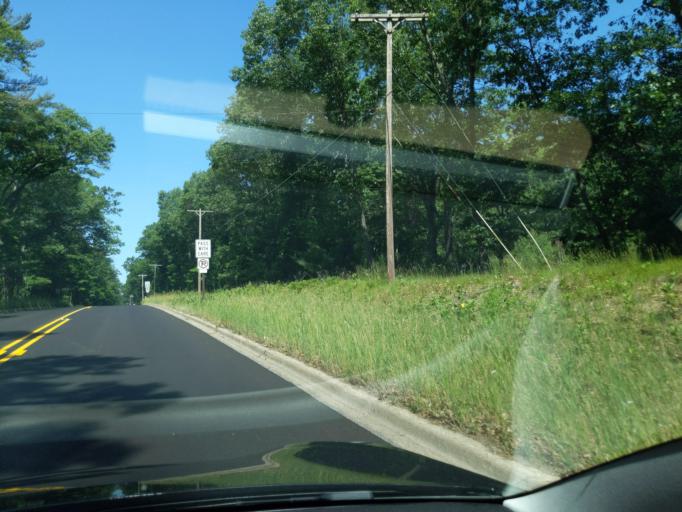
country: US
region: Michigan
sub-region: Muskegon County
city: Montague
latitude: 43.3821
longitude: -86.3993
